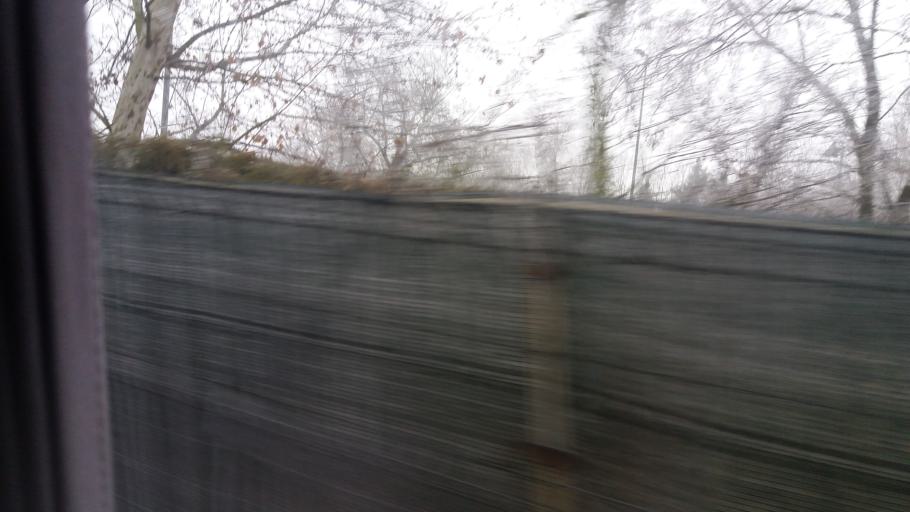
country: RO
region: Giurgiu
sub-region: Comuna Ogrezeni
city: Ogrezeni
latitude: 44.4033
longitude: 25.7811
